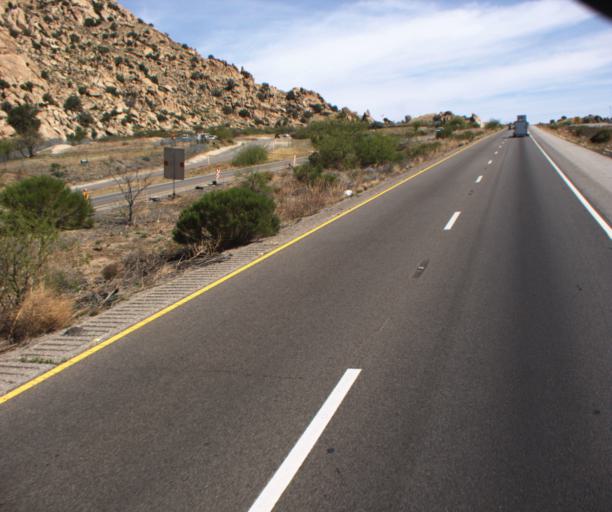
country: US
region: Arizona
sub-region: Cochise County
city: Saint David
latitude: 32.0578
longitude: -110.0793
